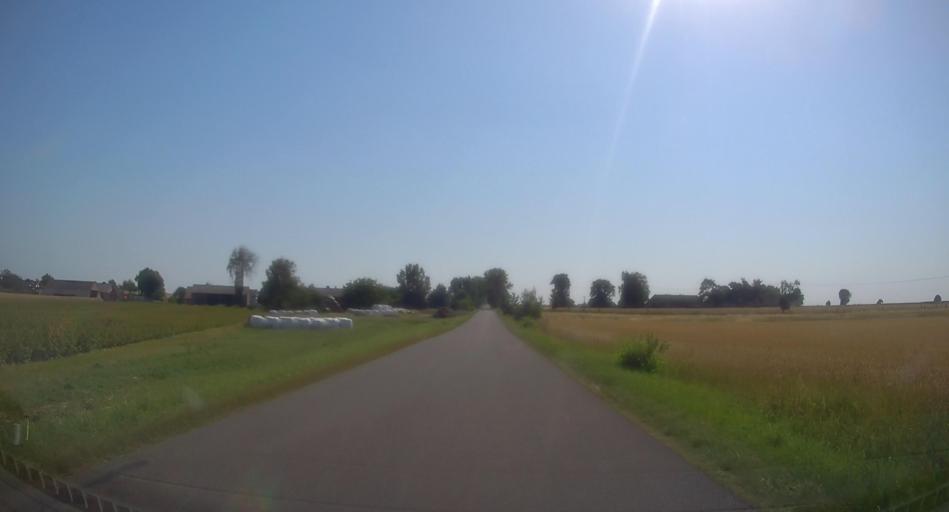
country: PL
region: Lodz Voivodeship
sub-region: Powiat skierniewicki
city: Kaweczyn Nowy
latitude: 51.8779
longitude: 20.2143
